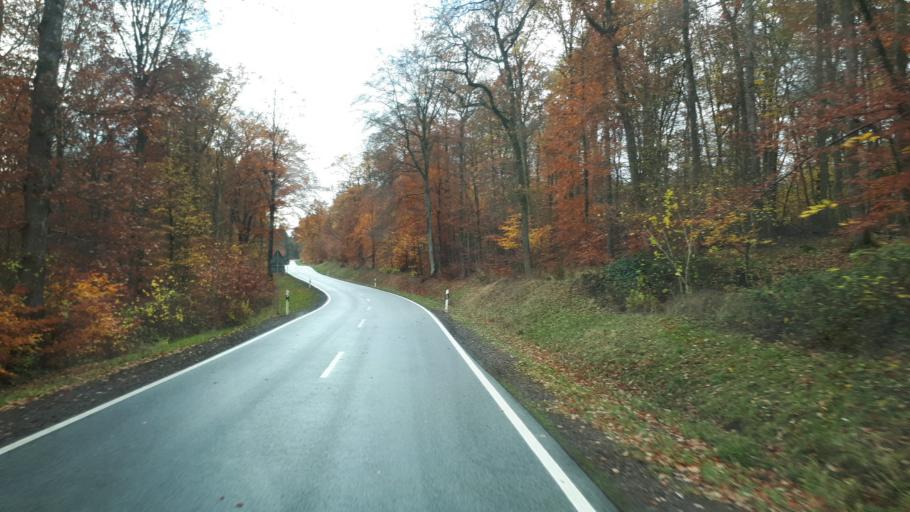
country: DE
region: Rheinland-Pfalz
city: Leienkaul
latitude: 50.1968
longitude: 7.0850
